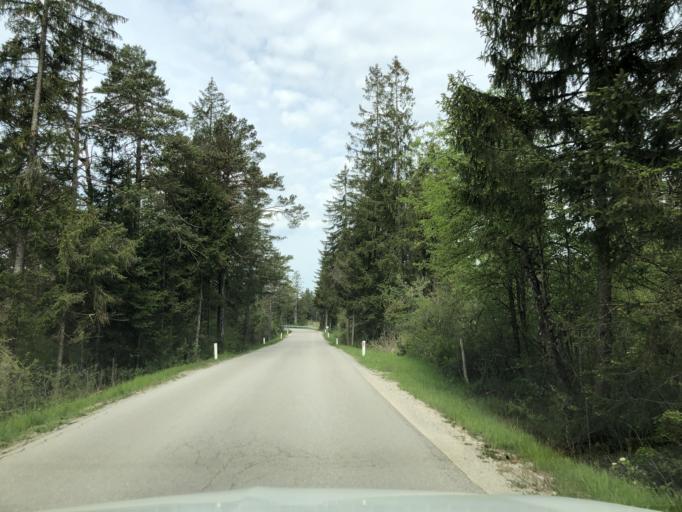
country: SI
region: Bloke
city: Nova Vas
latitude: 45.7937
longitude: 14.5123
